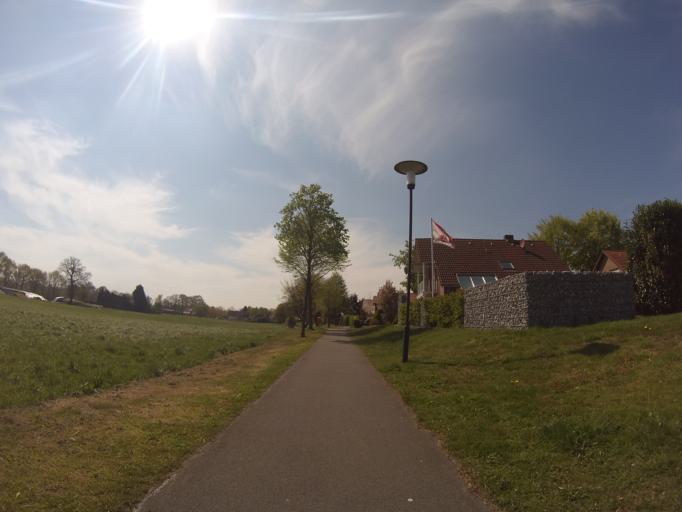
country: DE
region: Lower Saxony
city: Emlichheim
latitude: 52.6063
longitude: 6.8615
